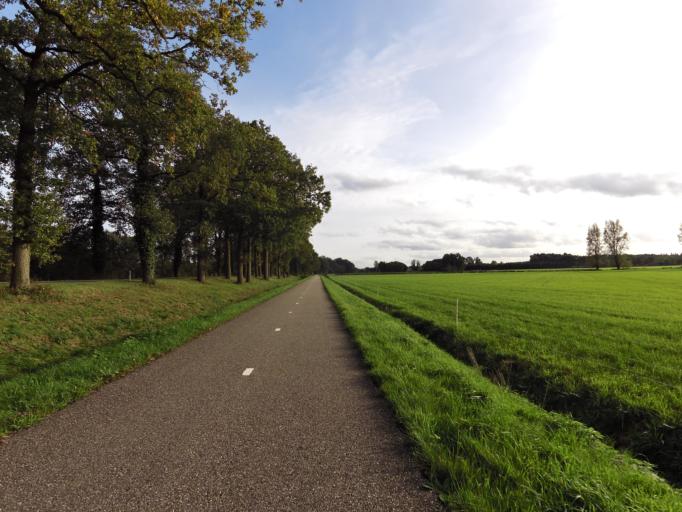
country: NL
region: Gelderland
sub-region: Gemeente Bronckhorst
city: Baak
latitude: 52.0196
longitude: 6.2225
